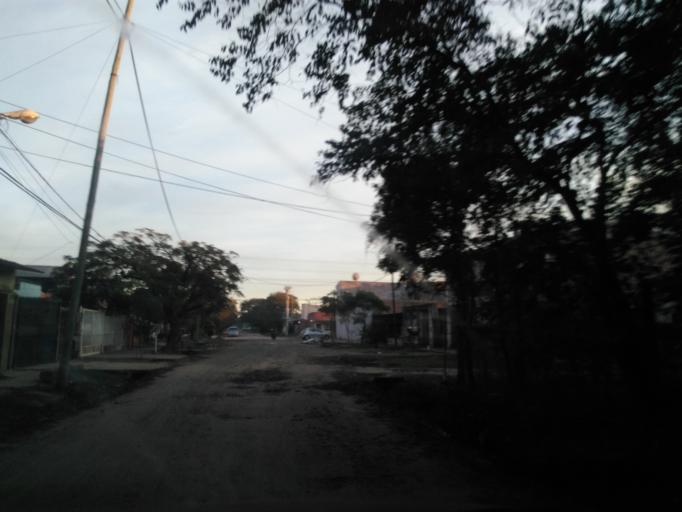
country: AR
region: Chaco
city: Resistencia
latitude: -27.4676
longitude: -58.9984
